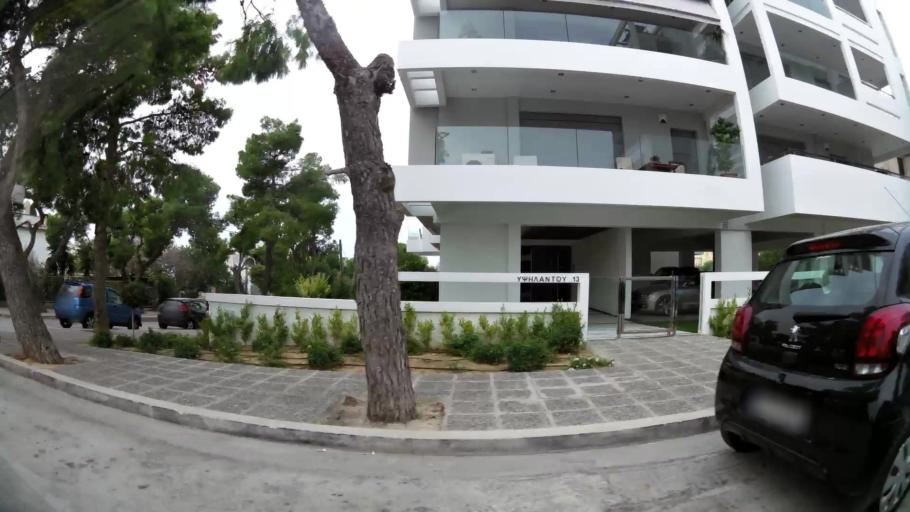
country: GR
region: Attica
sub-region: Nomarchia Athinas
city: Alimos
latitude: 37.9123
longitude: 23.7178
